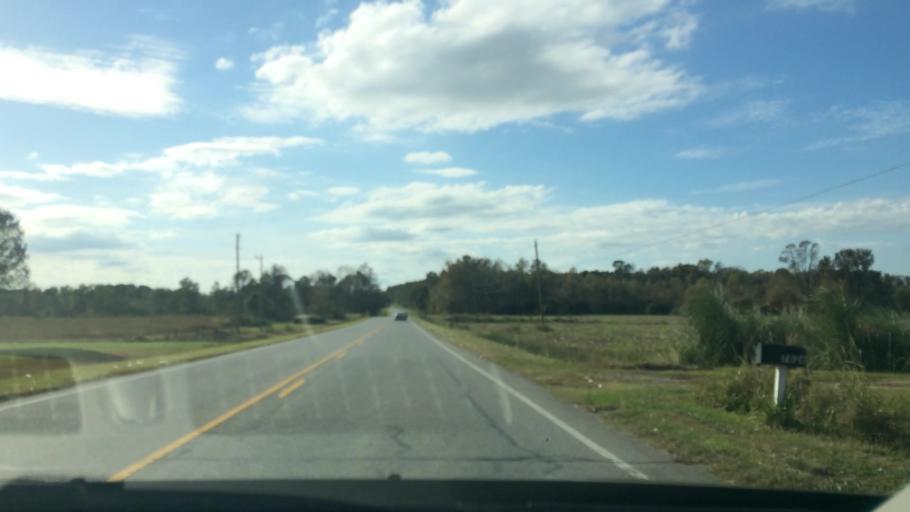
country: US
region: North Carolina
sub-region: Greene County
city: Snow Hill
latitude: 35.4419
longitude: -77.8123
